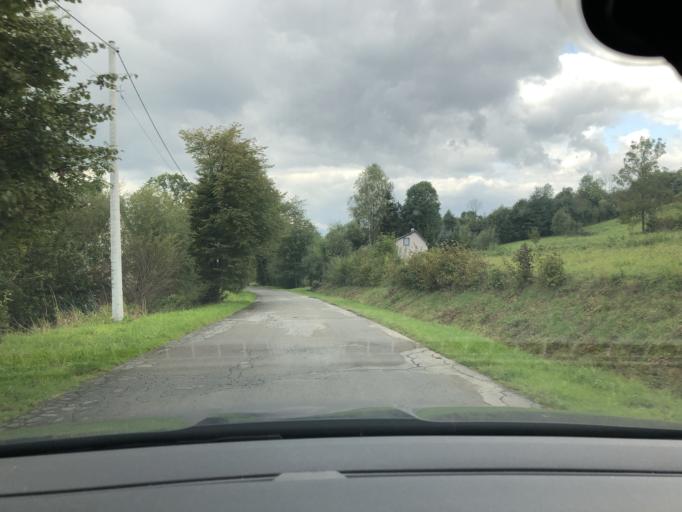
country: PL
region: Silesian Voivodeship
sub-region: Powiat zywiecki
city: Slemien
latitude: 49.7261
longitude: 19.4050
